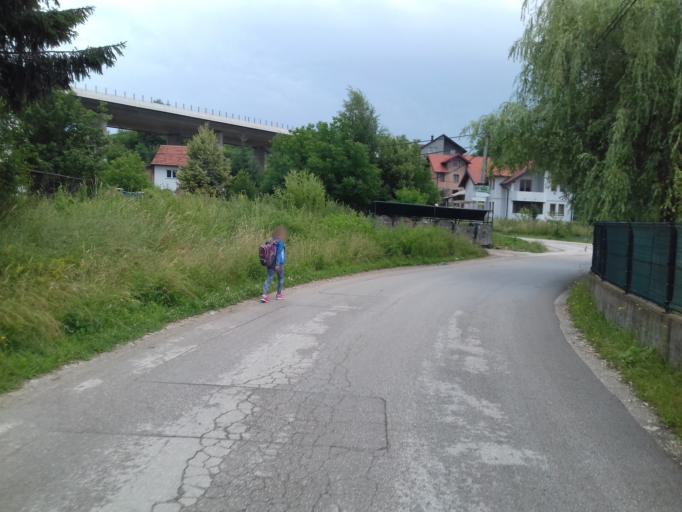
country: BA
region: Federation of Bosnia and Herzegovina
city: Hadzici
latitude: 43.8631
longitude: 18.2297
